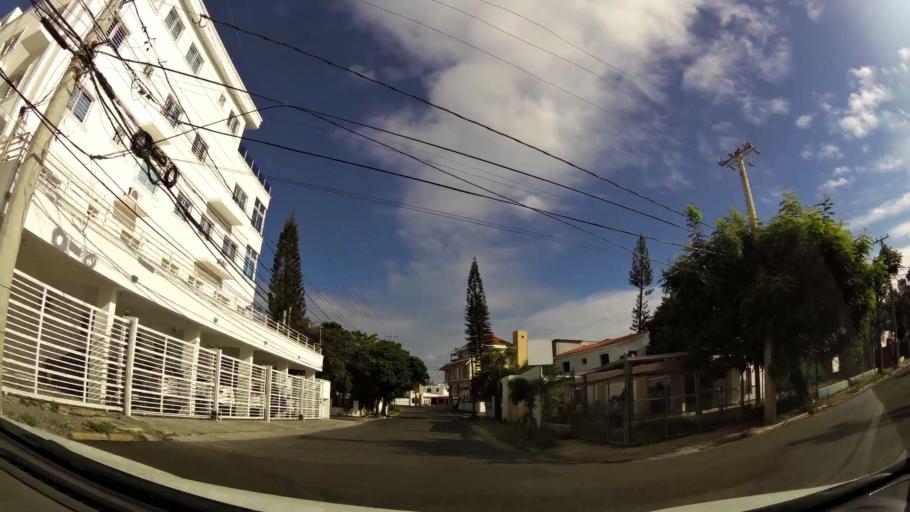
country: DO
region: Nacional
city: Bella Vista
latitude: 18.4653
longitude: -69.9540
